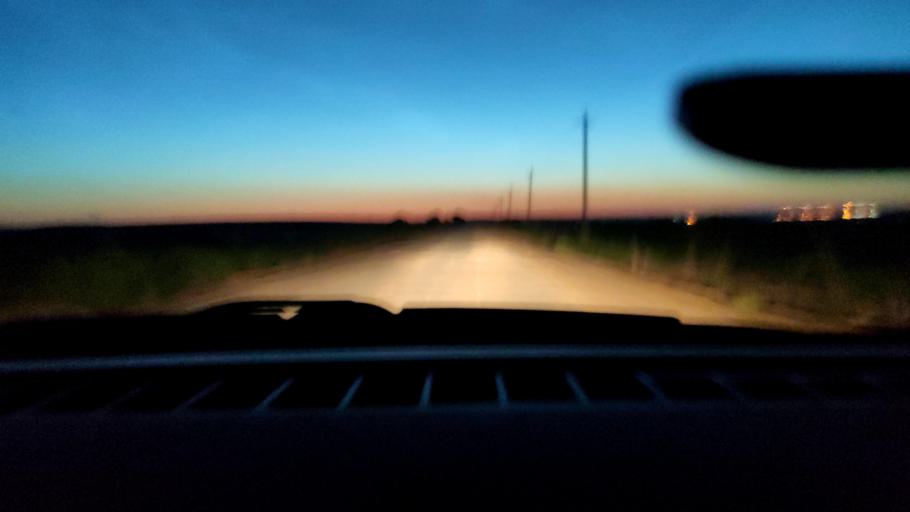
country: RU
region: Perm
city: Kultayevo
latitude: 57.8538
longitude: 55.9848
